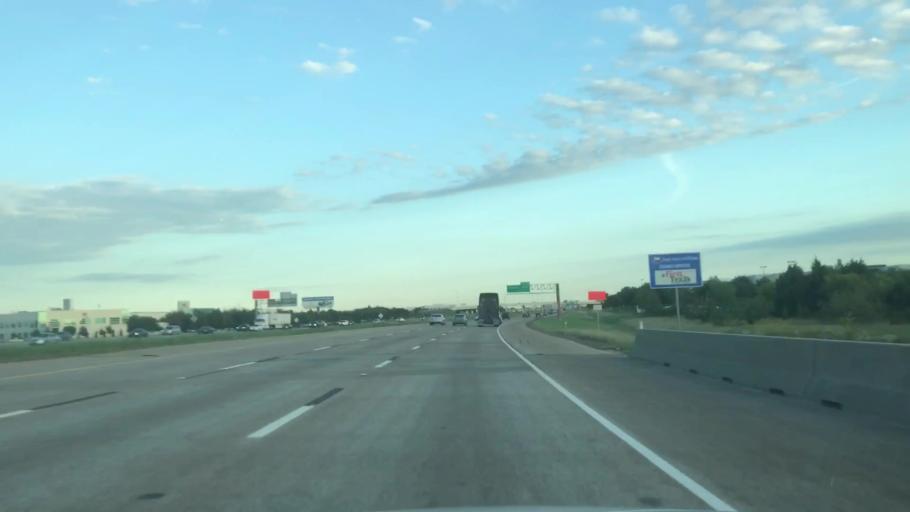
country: US
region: Texas
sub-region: Dallas County
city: Coppell
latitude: 32.9409
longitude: -97.0139
